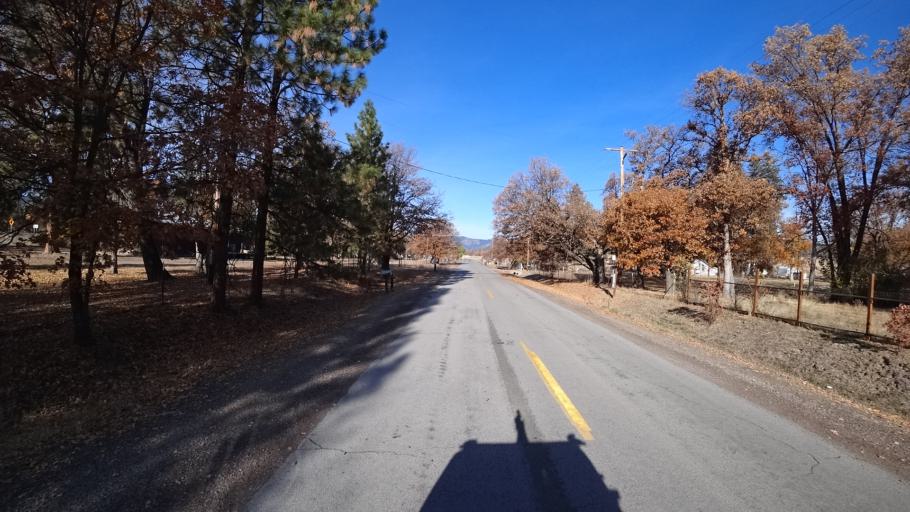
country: US
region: California
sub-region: Siskiyou County
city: Yreka
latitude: 41.6667
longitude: -122.6059
